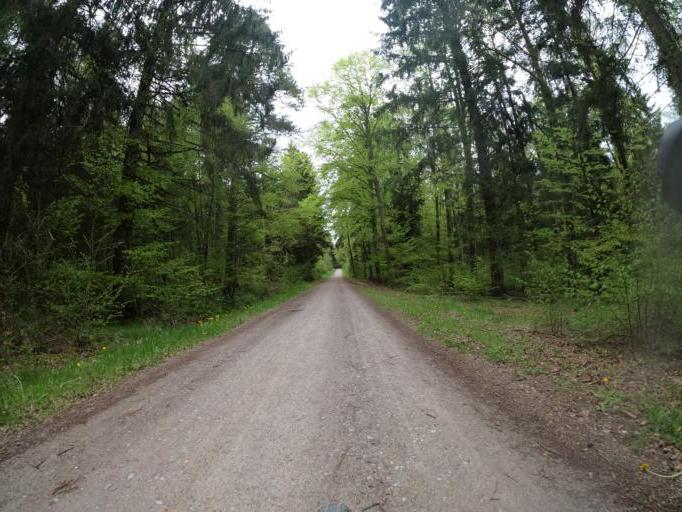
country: DE
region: Baden-Wuerttemberg
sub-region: Karlsruhe Region
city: Rohrdorf
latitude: 48.5487
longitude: 8.6943
